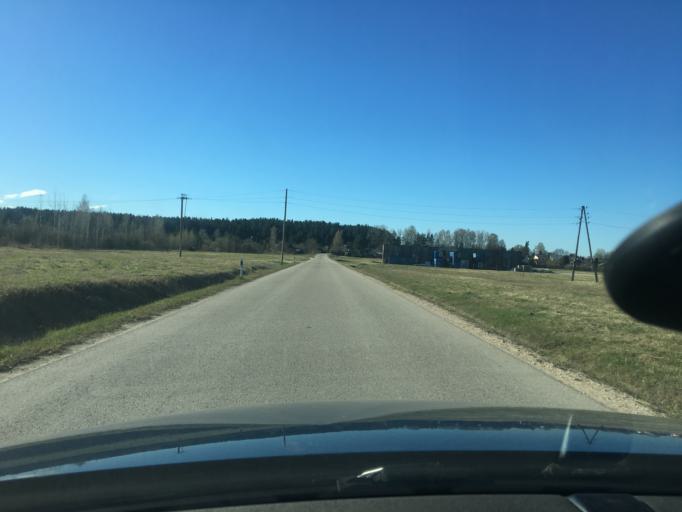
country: LV
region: Kekava
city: Kekava
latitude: 56.8514
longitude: 24.2606
